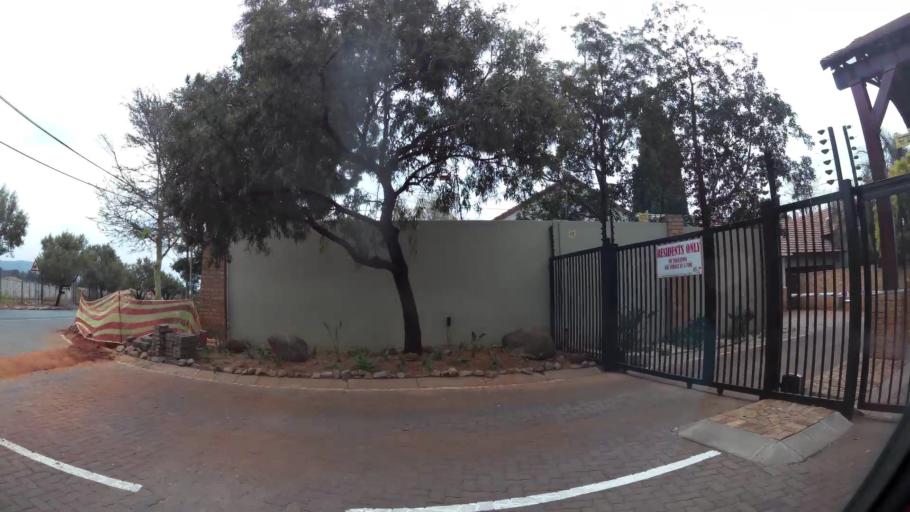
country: ZA
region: Gauteng
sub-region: West Rand District Municipality
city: Muldersdriseloop
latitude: -26.0891
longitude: 27.8734
